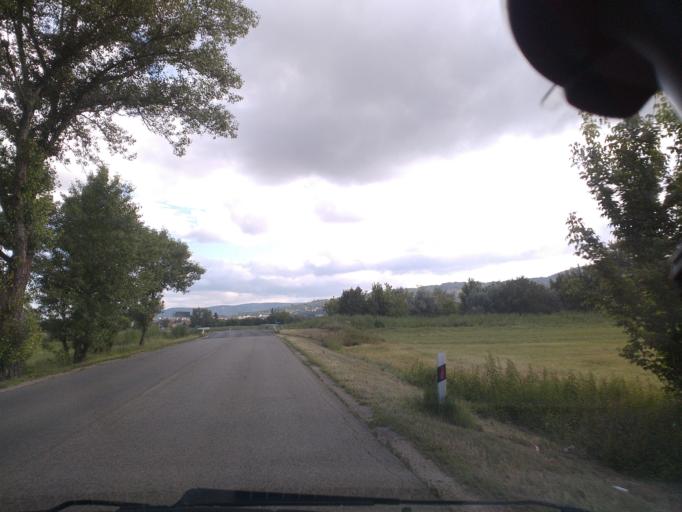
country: HU
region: Komarom-Esztergom
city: Esztergom
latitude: 47.7630
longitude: 18.7368
